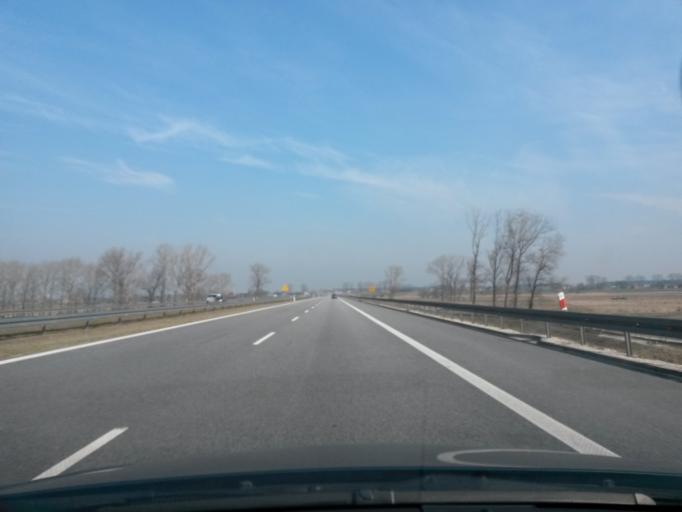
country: PL
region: Lodz Voivodeship
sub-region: Powiat kutnowski
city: Krzyzanow
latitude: 52.1704
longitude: 19.4851
